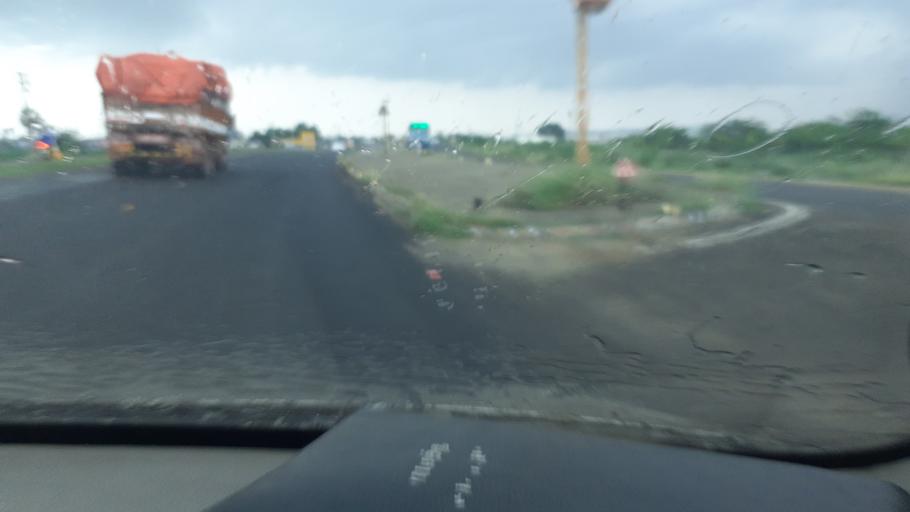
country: IN
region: Tamil Nadu
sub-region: Thoothukkudi
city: Kovilpatti
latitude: 9.1006
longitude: 77.8077
